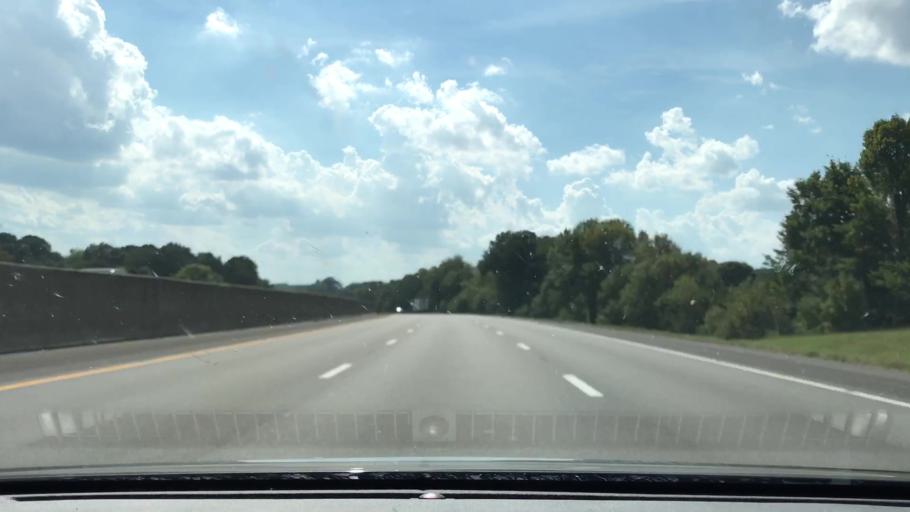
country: US
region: Kentucky
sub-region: Warren County
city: Bowling Green
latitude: 36.9940
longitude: -86.3817
